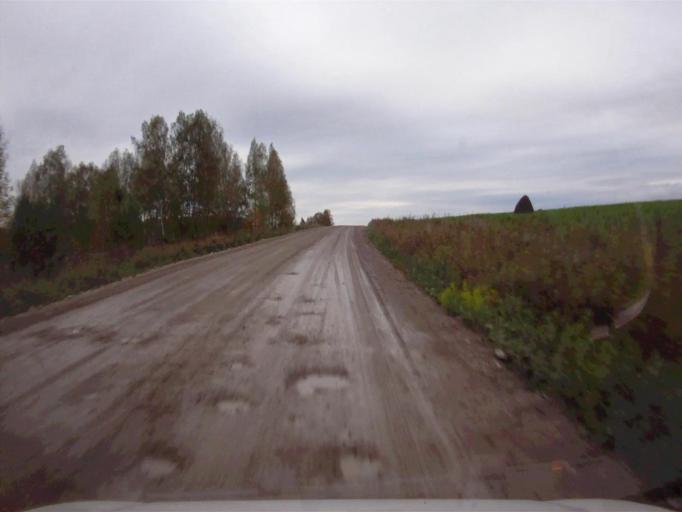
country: RU
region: Sverdlovsk
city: Mikhaylovsk
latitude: 56.1775
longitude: 59.2062
